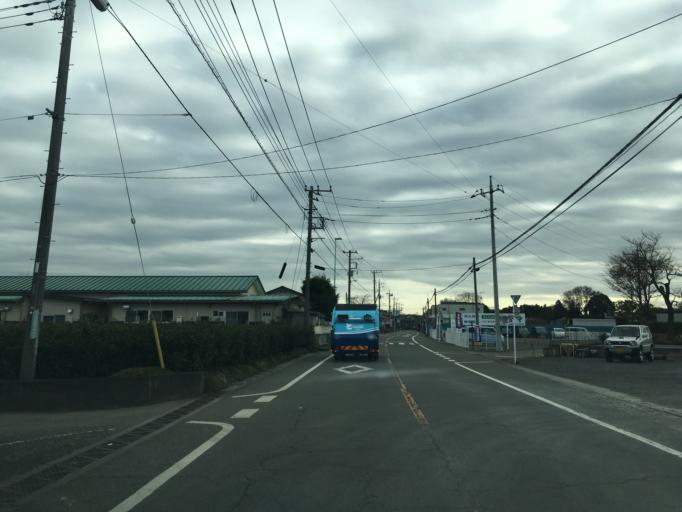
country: JP
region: Saitama
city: Sayama
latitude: 35.7968
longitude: 139.3973
